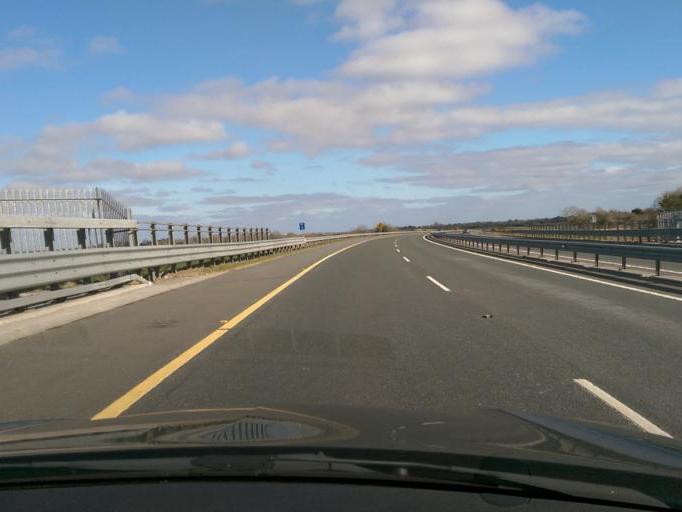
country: IE
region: Leinster
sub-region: An Iarmhi
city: Athlone
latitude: 53.3980
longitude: -8.0478
